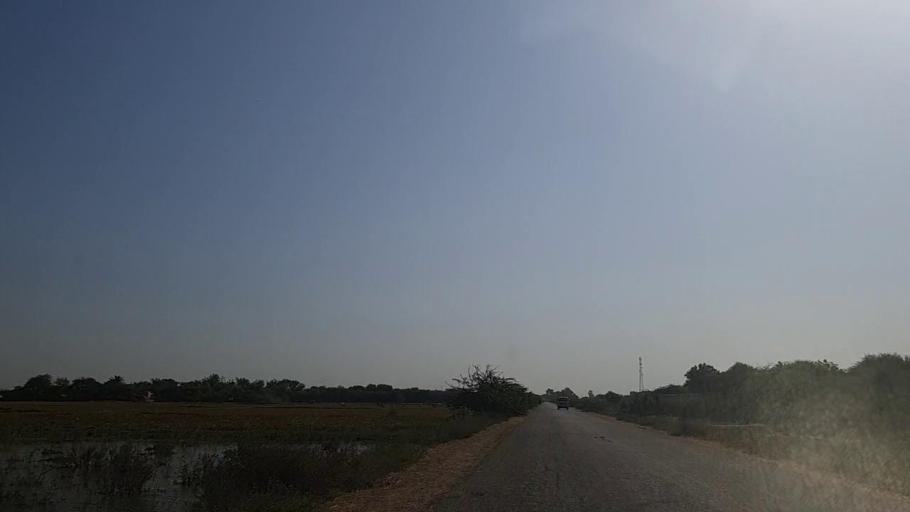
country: PK
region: Sindh
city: Jati
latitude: 24.5228
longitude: 68.2766
